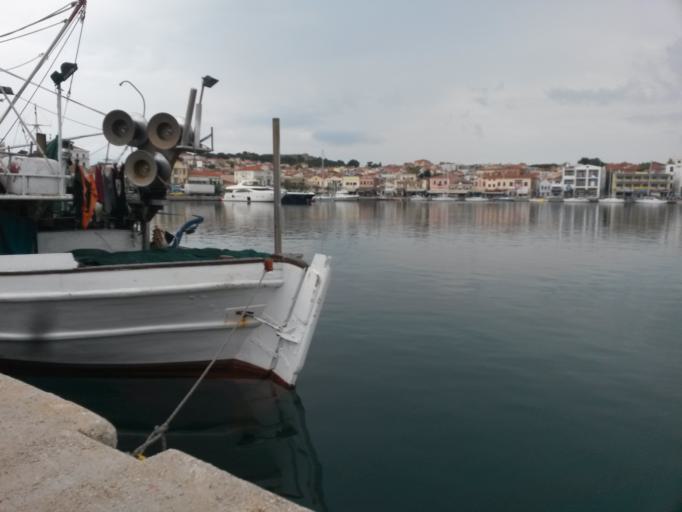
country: GR
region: North Aegean
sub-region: Nomos Lesvou
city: Mytilini
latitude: 39.1050
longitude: 26.5557
